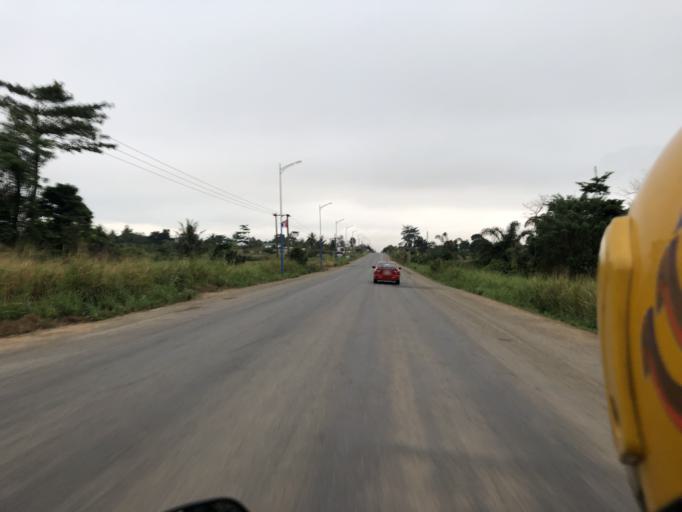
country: GH
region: Eastern
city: Koforidua
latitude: 6.1851
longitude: -0.3519
